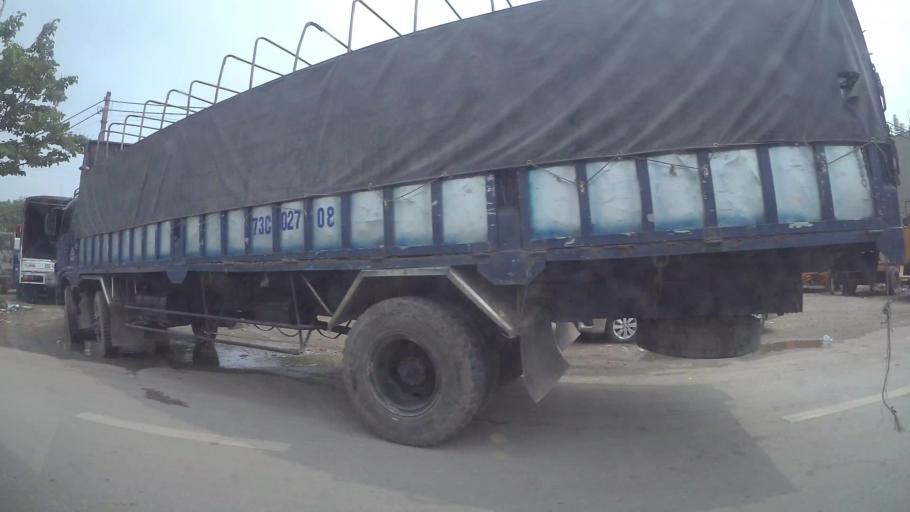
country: VN
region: Ha Noi
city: Van Dien
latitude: 20.9646
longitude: 105.8591
